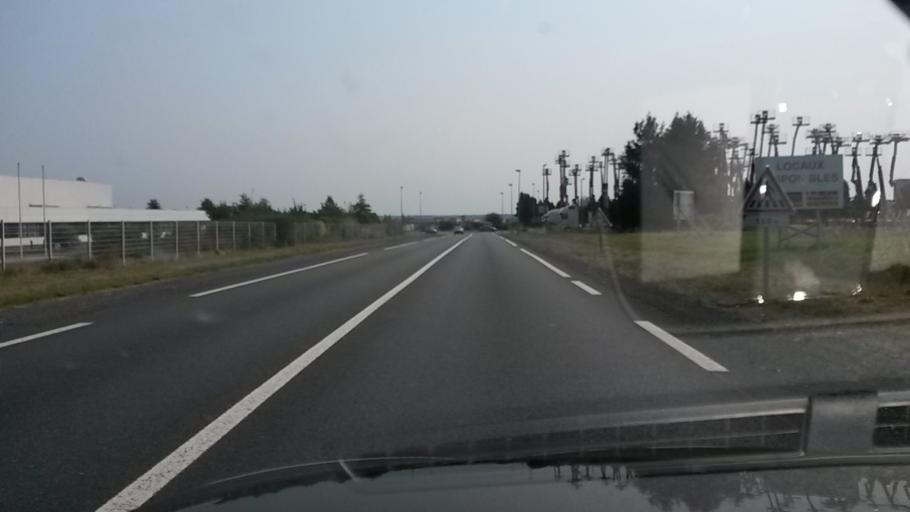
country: FR
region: Pays de la Loire
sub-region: Departement de la Loire-Atlantique
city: Mesanger
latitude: 47.4119
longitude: -1.1900
